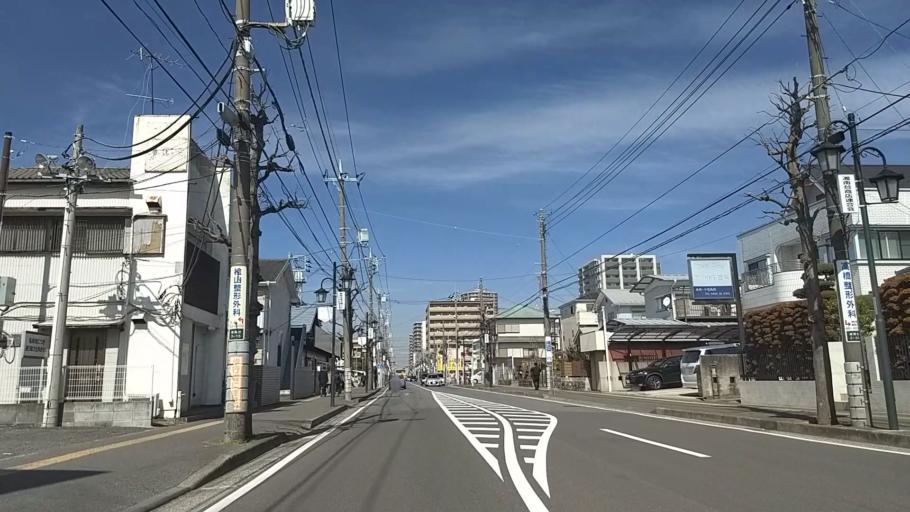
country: JP
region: Kanagawa
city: Fujisawa
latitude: 35.3925
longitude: 139.4640
